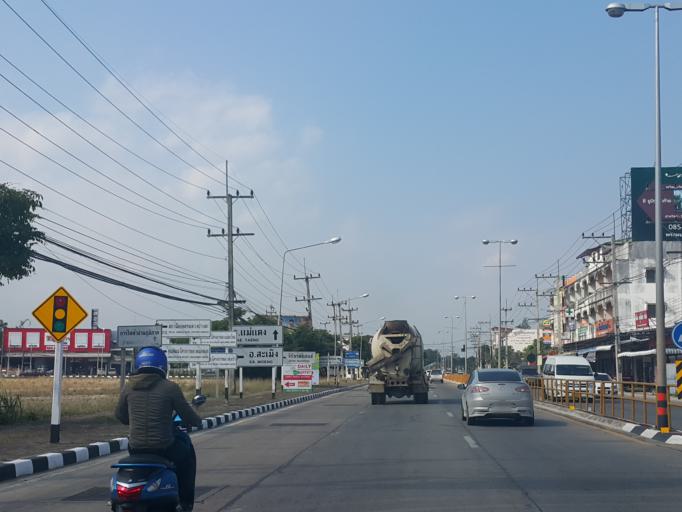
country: TH
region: Chiang Mai
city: San Sai
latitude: 18.9215
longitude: 98.9412
